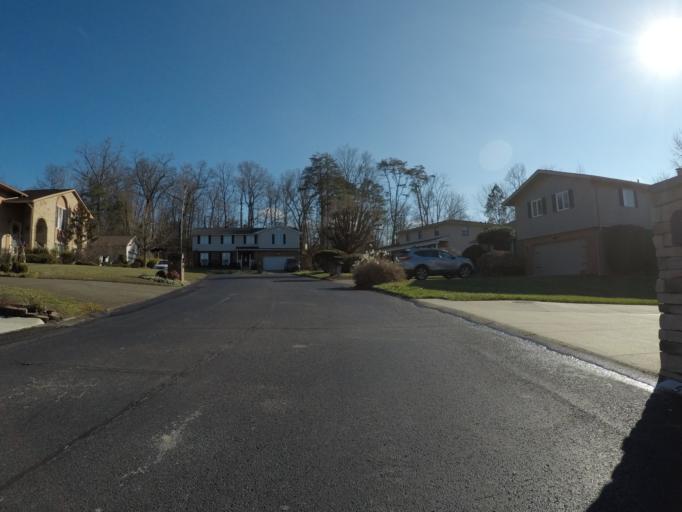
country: US
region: West Virginia
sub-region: Cabell County
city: Pea Ridge
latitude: 38.4162
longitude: -82.3254
